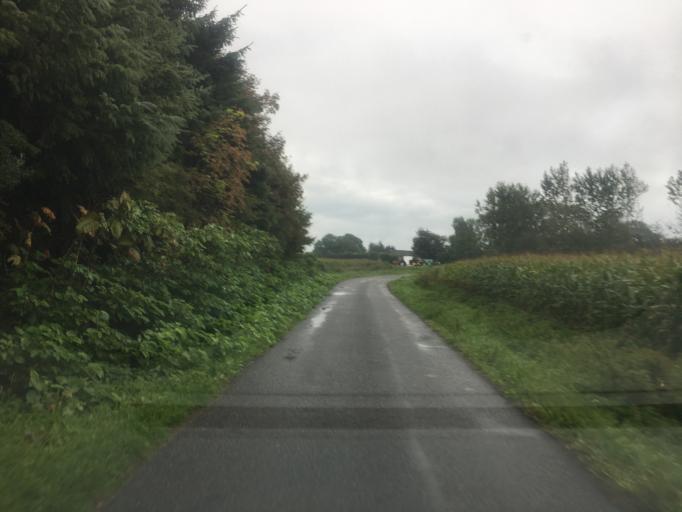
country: DK
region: South Denmark
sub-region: Tonder Kommune
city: Logumkloster
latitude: 54.9814
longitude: 8.9600
